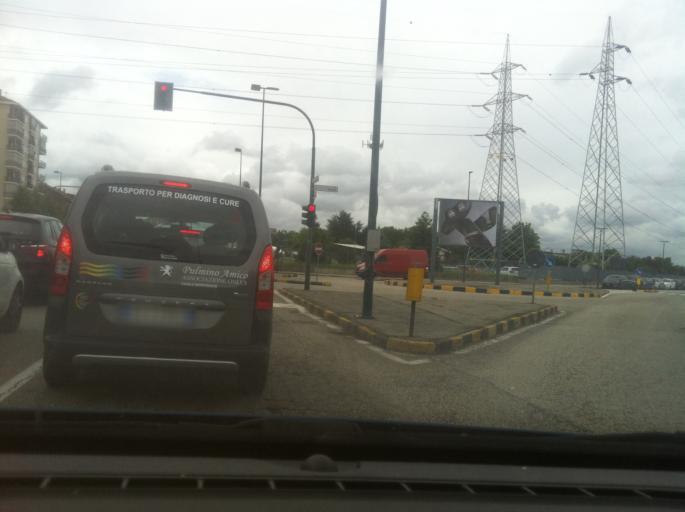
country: IT
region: Piedmont
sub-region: Provincia di Torino
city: San Mauro Torinese
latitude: 45.1081
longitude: 7.7282
